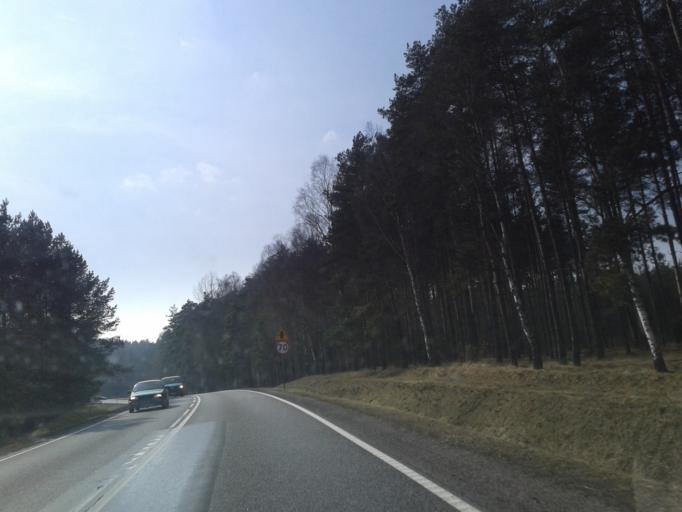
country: PL
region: Pomeranian Voivodeship
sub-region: Powiat czluchowski
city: Czarne
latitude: 53.5598
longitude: 17.0291
